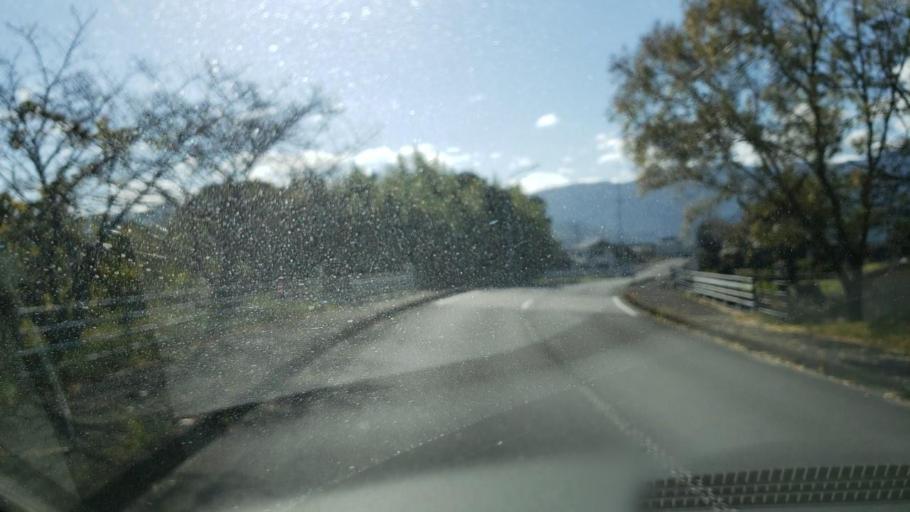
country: JP
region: Tokushima
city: Wakimachi
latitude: 34.0803
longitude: 134.2367
